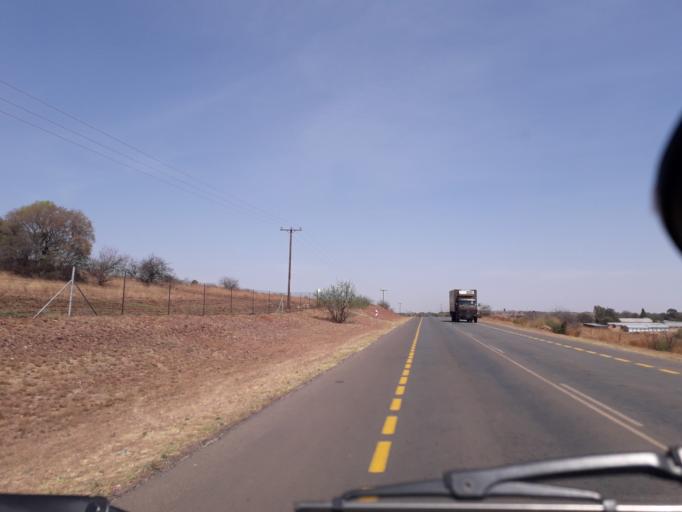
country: ZA
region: Gauteng
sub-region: West Rand District Municipality
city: Krugersdorp
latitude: -26.0180
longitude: 27.7285
